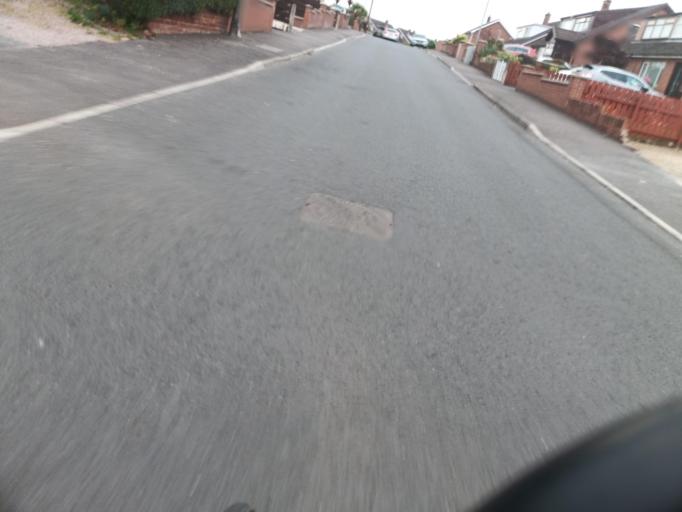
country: GB
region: Northern Ireland
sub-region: Ards District
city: Comber
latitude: 54.5553
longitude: -5.7336
